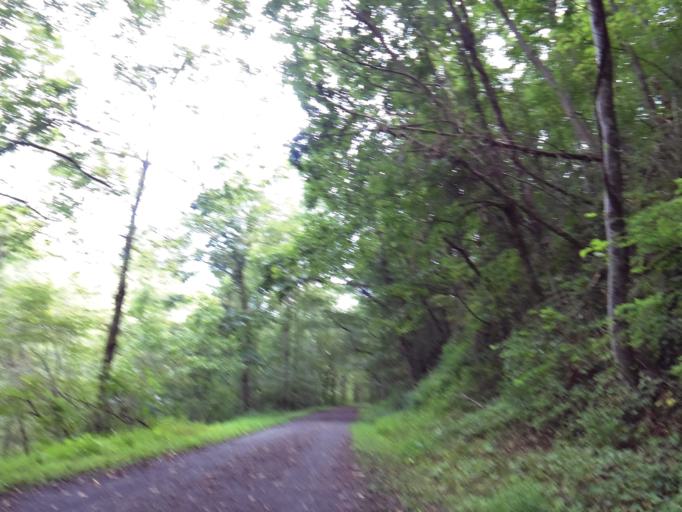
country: US
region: Virginia
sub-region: Washington County
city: Abingdon
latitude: 36.6945
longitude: -81.9409
